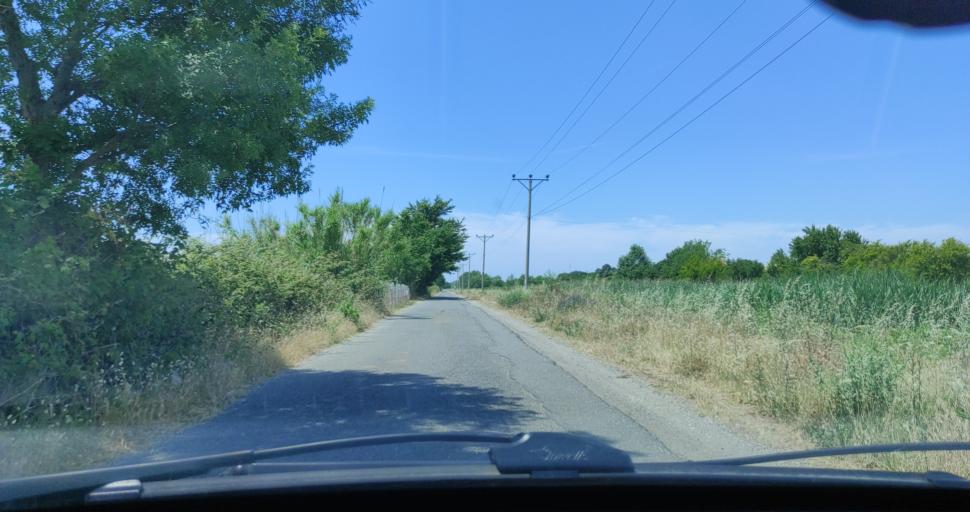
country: AL
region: Shkoder
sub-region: Rrethi i Shkodres
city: Velipoje
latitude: 41.8789
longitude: 19.3980
